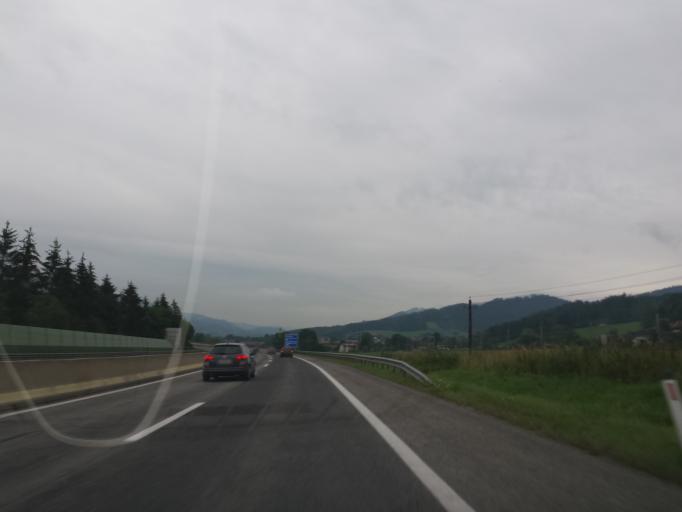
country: AT
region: Styria
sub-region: Politischer Bezirk Bruck-Muerzzuschlag
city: Muerzhofen
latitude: 47.4716
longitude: 15.3880
